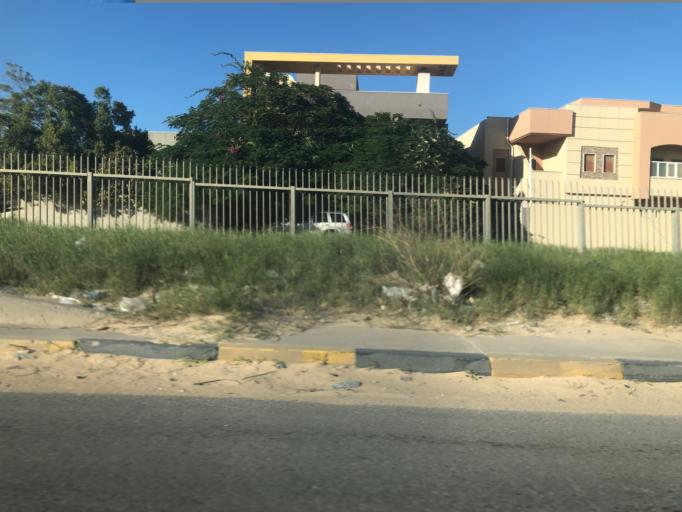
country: LY
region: Tripoli
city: Tripoli
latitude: 32.8698
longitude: 13.2626
